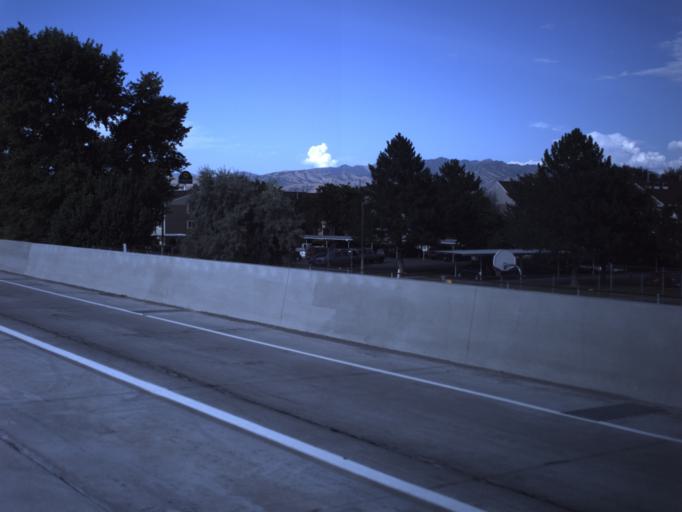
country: US
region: Utah
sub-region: Salt Lake County
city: Taylorsville
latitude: 40.6933
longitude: -111.9518
